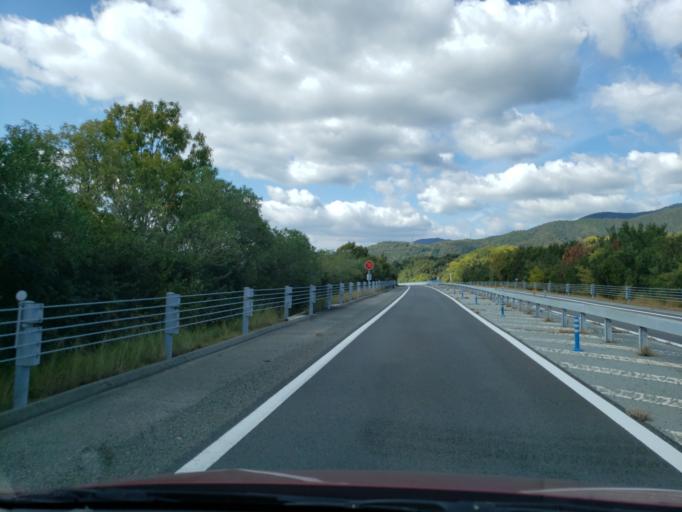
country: JP
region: Tokushima
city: Kamojimacho-jogejima
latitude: 34.1219
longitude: 134.3661
